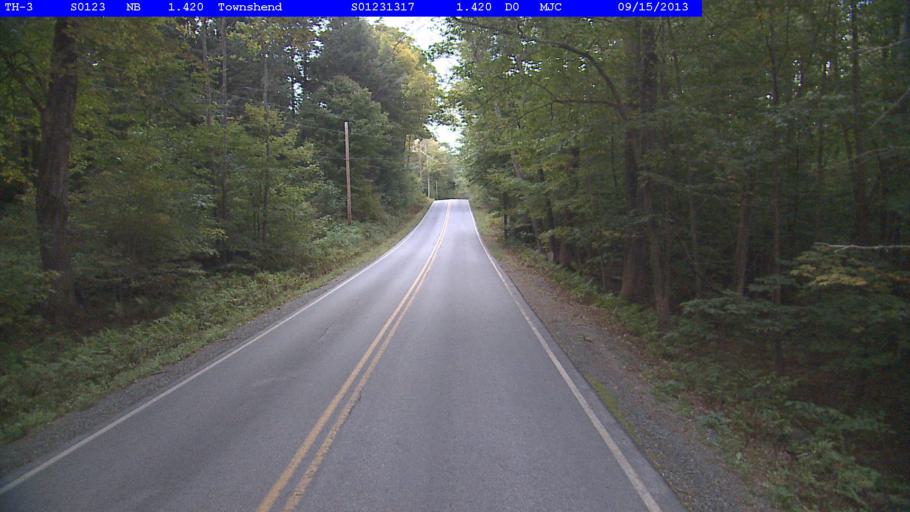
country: US
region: Vermont
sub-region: Windham County
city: Newfane
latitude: 43.1032
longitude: -72.7091
